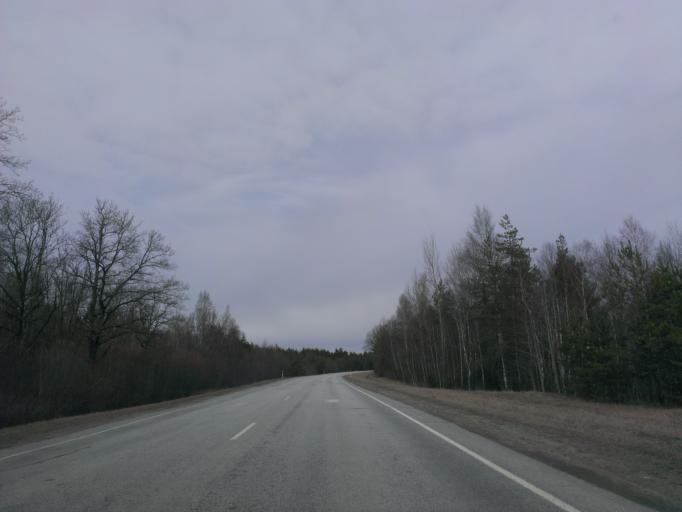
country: EE
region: Laeaene
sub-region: Lihula vald
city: Lihula
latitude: 58.6011
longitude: 23.5538
